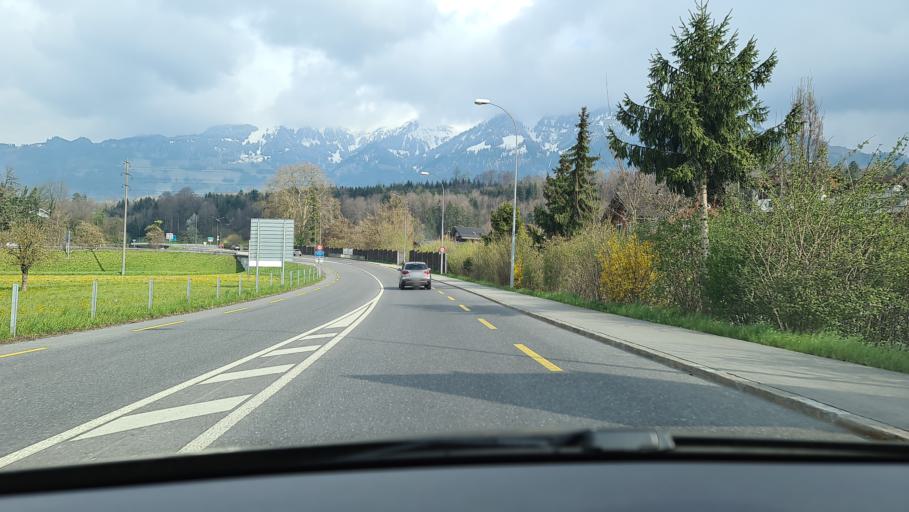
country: CH
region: Obwalden
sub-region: Obwalden
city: Sarnen
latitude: 46.8970
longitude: 8.2537
